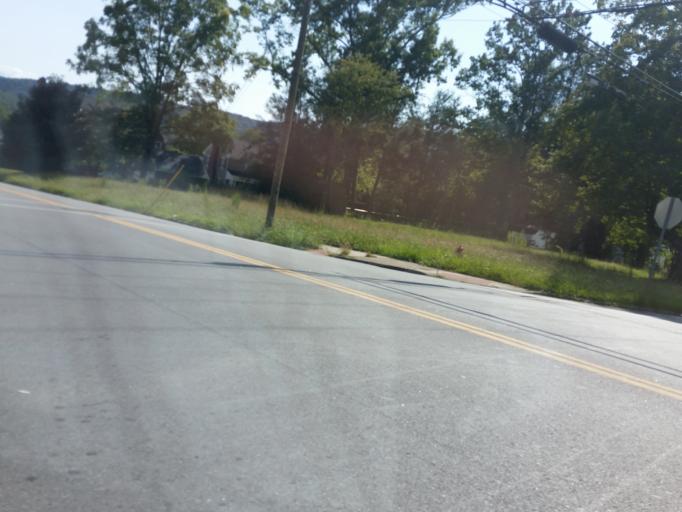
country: US
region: Kentucky
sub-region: Bell County
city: Middlesboro
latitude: 36.6087
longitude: -83.7223
